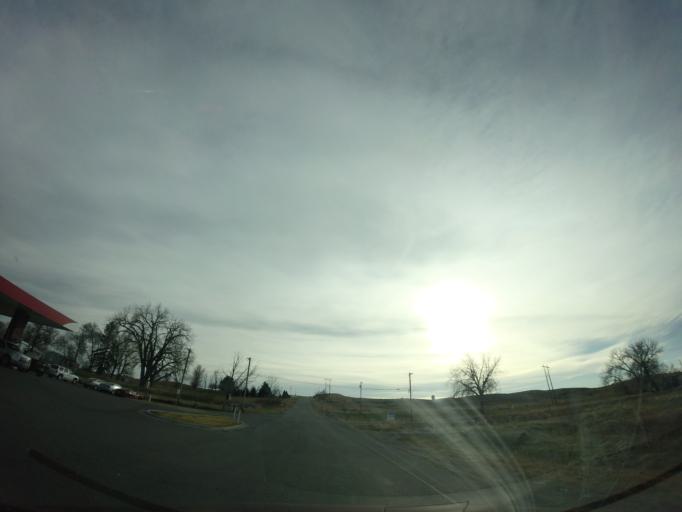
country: US
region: Montana
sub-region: Yellowstone County
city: Billings
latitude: 45.7954
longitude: -108.4555
